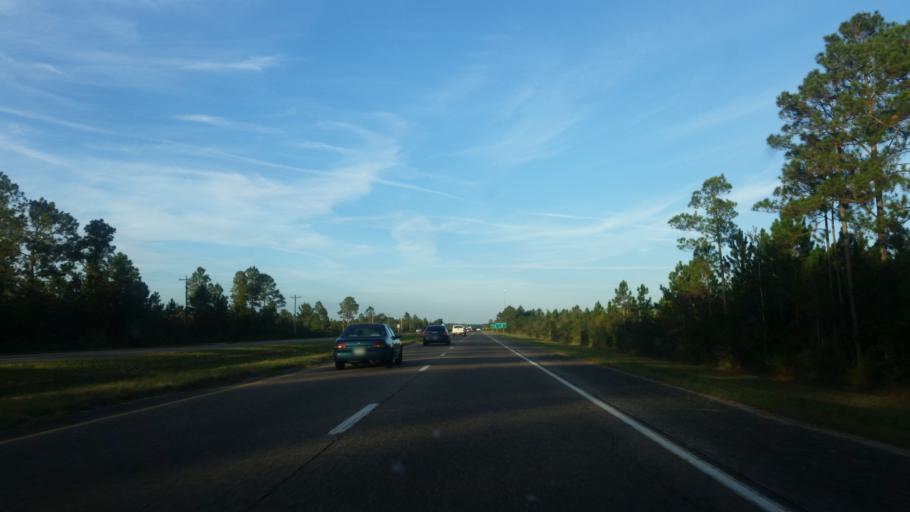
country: US
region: Mississippi
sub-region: Jackson County
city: Helena
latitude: 30.4516
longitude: -88.4231
